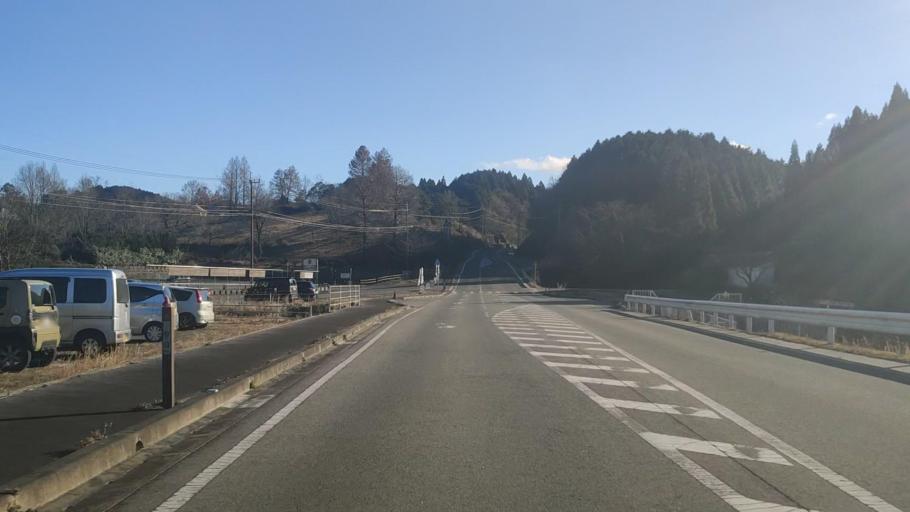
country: JP
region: Saga Prefecture
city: Kanzakimachi-kanzaki
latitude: 33.4069
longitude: 130.2722
